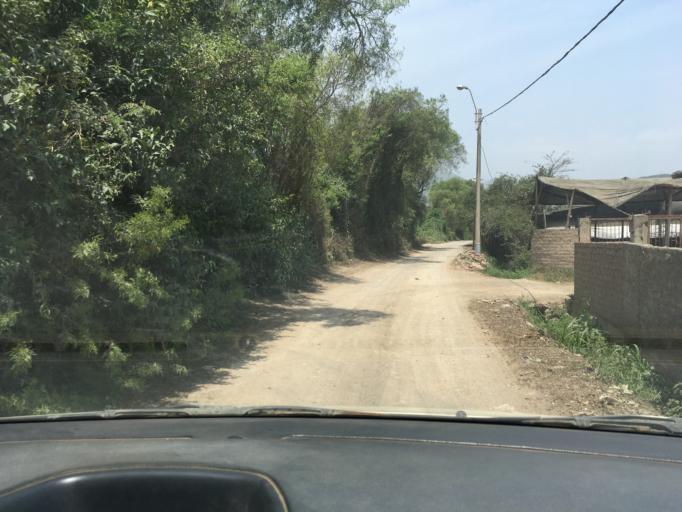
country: PE
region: Lima
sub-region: Lima
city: Cieneguilla
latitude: -12.1876
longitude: -76.8646
